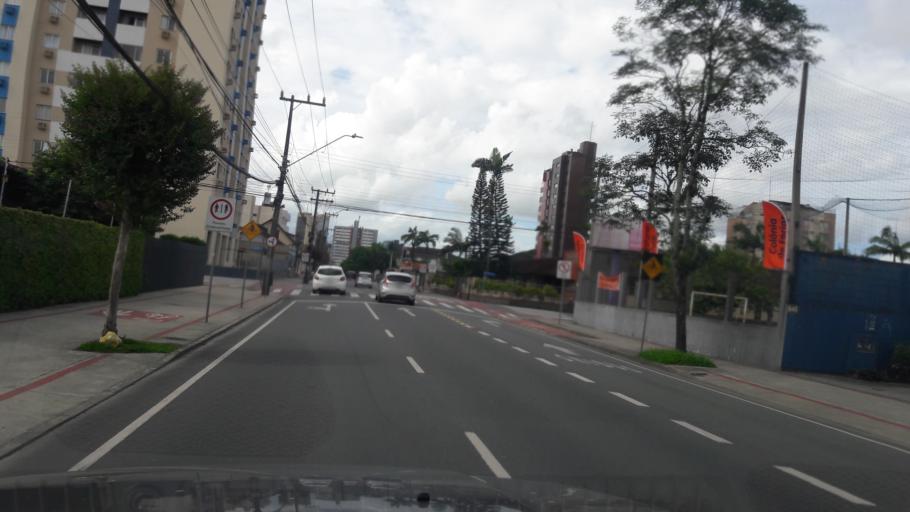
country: BR
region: Santa Catarina
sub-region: Joinville
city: Joinville
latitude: -26.3134
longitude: -48.8428
